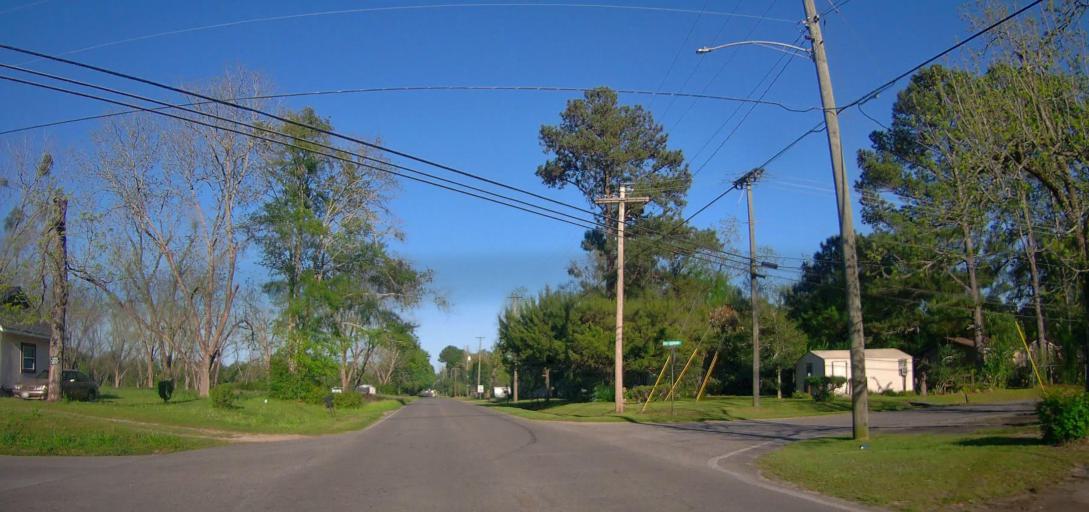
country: US
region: Georgia
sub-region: Ben Hill County
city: Fitzgerald
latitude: 31.7239
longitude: -83.2505
